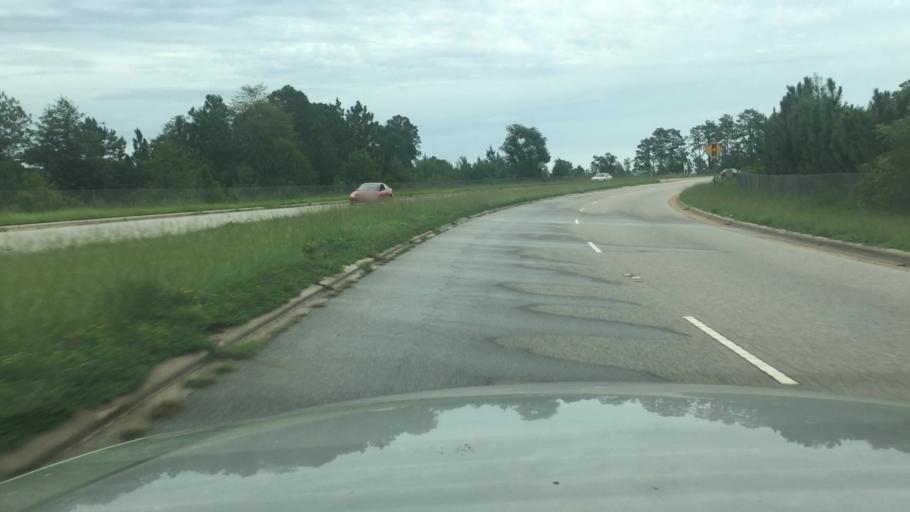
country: US
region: North Carolina
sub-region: Cumberland County
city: Hope Mills
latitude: 34.9920
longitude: -78.9516
